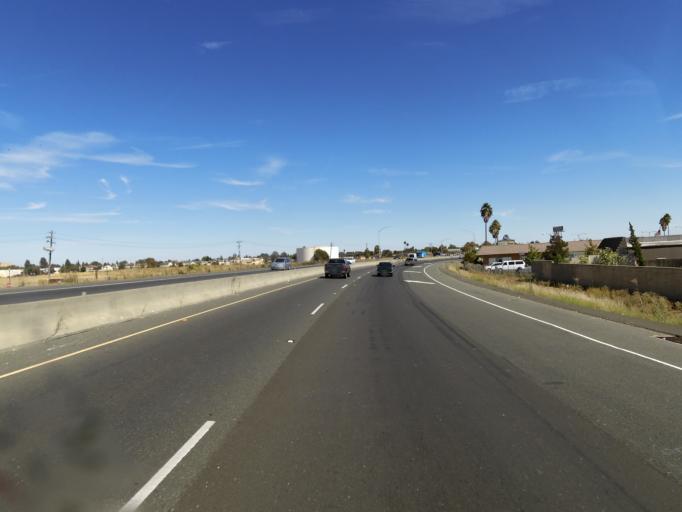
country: US
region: California
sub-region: Solano County
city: Fairfield
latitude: 38.2448
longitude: -122.0371
